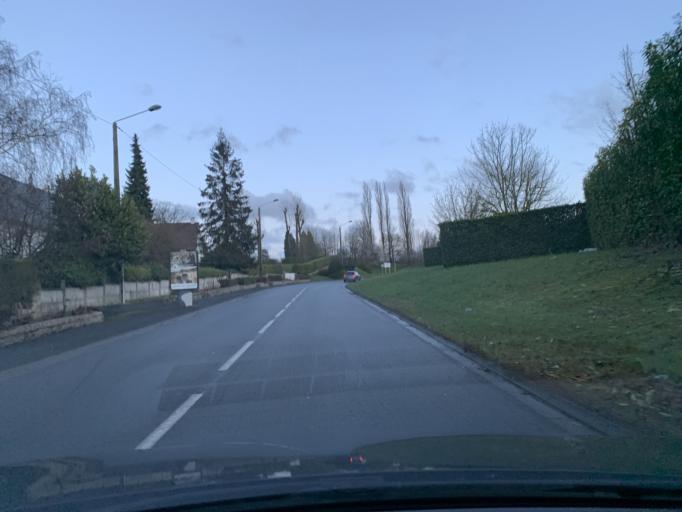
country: FR
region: Nord-Pas-de-Calais
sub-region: Departement du Nord
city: Cambrai
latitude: 50.1567
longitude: 3.2573
